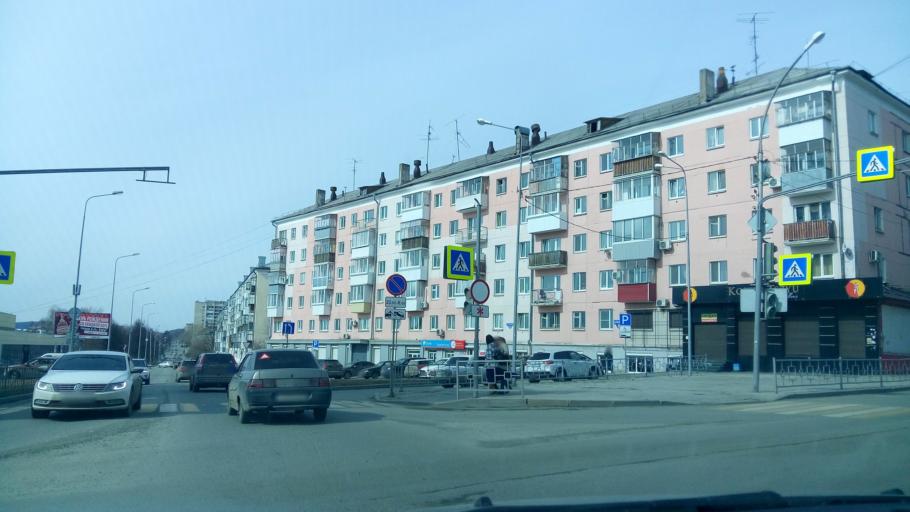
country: RU
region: Sverdlovsk
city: Nizhniy Tagil
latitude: 57.9058
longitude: 59.9845
